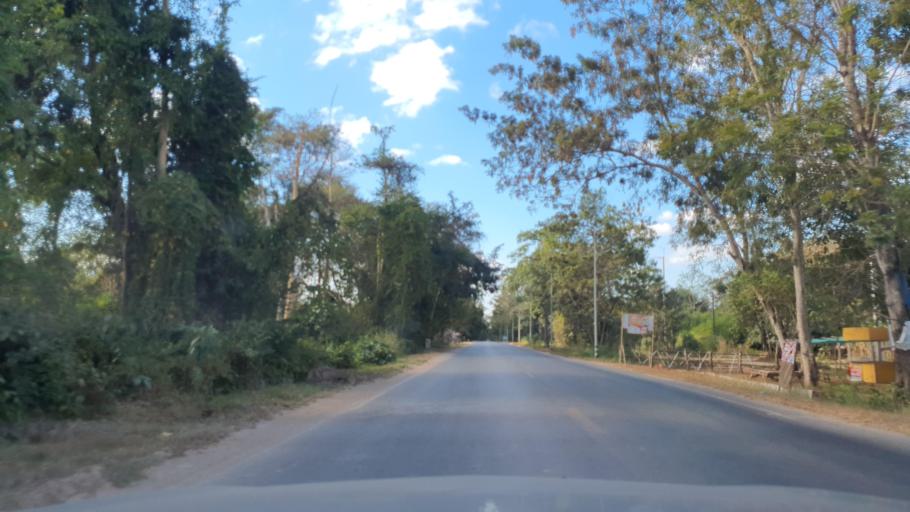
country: TH
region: Nakhon Phanom
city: Ban Phaeng
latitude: 18.0148
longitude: 104.1562
